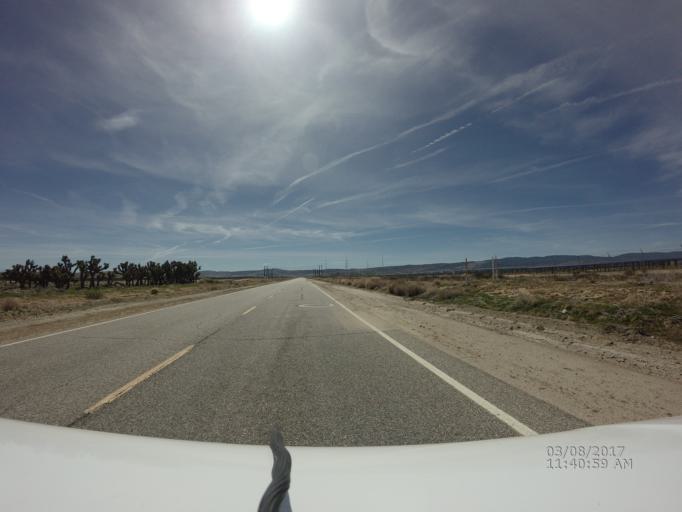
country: US
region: California
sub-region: Los Angeles County
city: Green Valley
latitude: 34.7905
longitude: -118.4314
